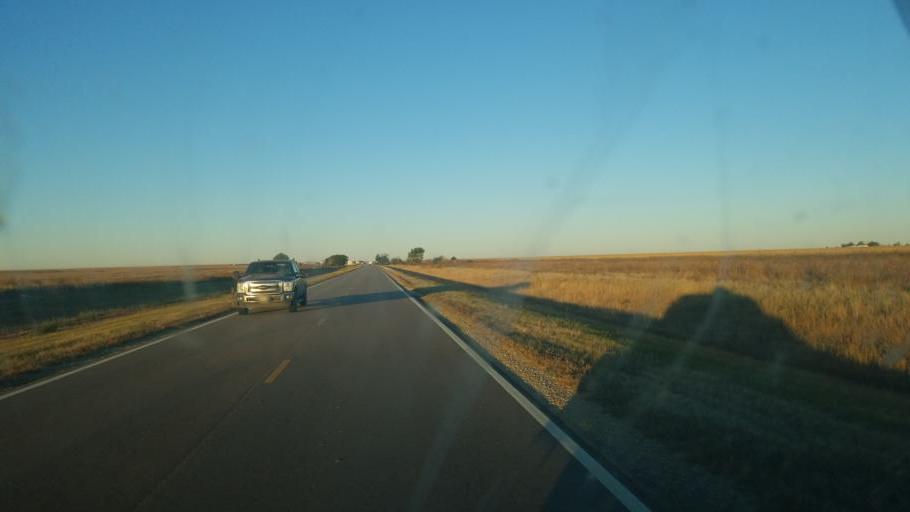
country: US
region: Kansas
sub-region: Wallace County
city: Sharon Springs
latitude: 38.8588
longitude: -102.0382
